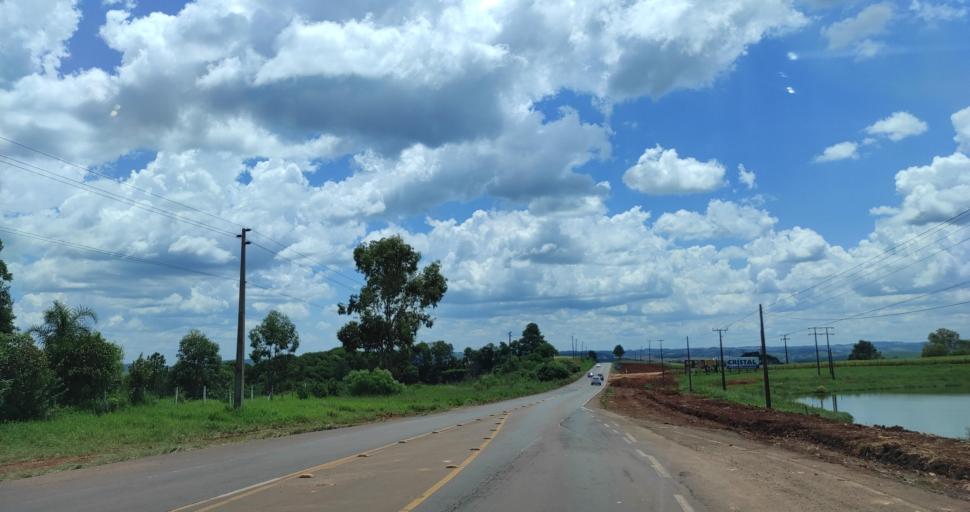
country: BR
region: Santa Catarina
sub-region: Xanxere
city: Xanxere
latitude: -26.7842
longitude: -52.4080
